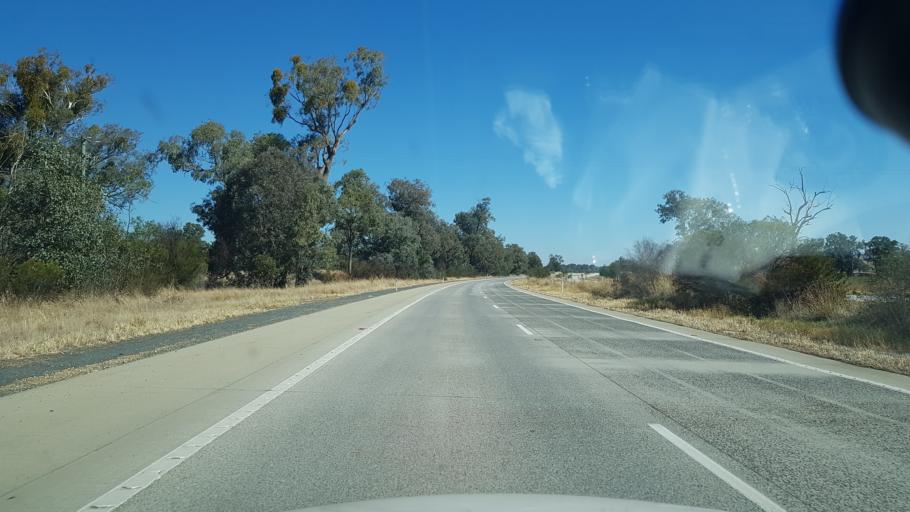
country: AU
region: New South Wales
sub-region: Greater Hume Shire
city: Holbrook
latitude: -35.9029
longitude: 147.1641
